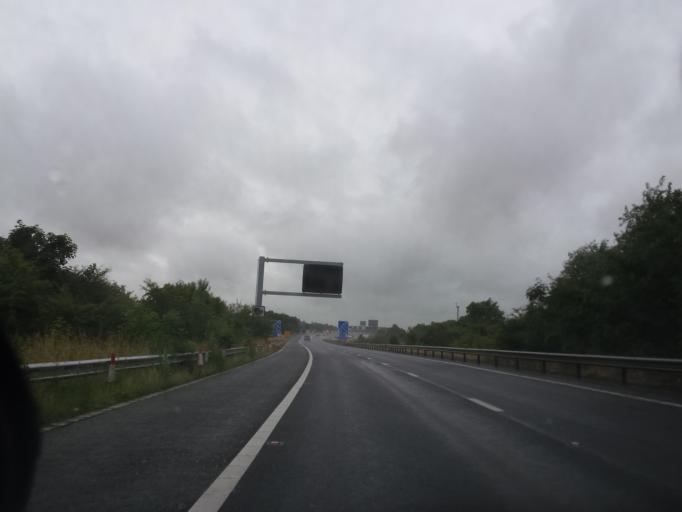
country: GB
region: England
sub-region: Rotherham
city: Ulley
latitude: 53.3855
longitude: -1.2775
